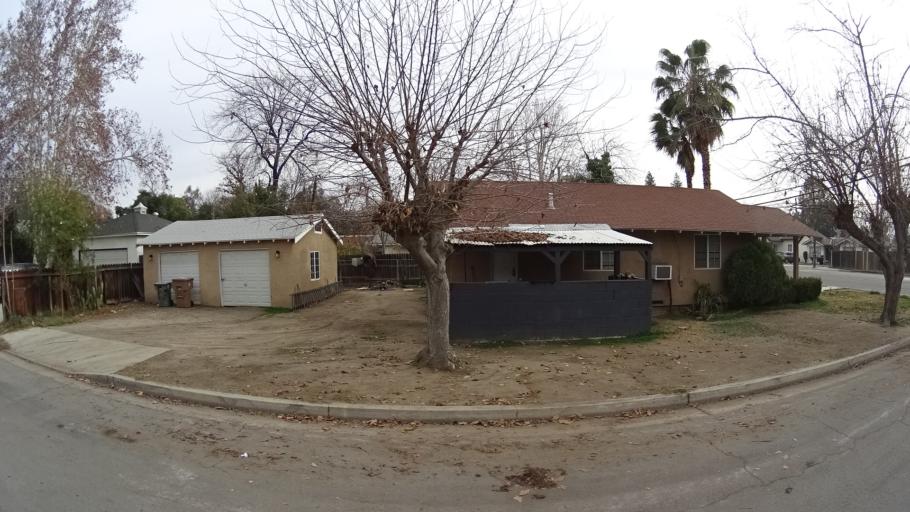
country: US
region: California
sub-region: Kern County
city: Bakersfield
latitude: 35.3615
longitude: -119.0271
